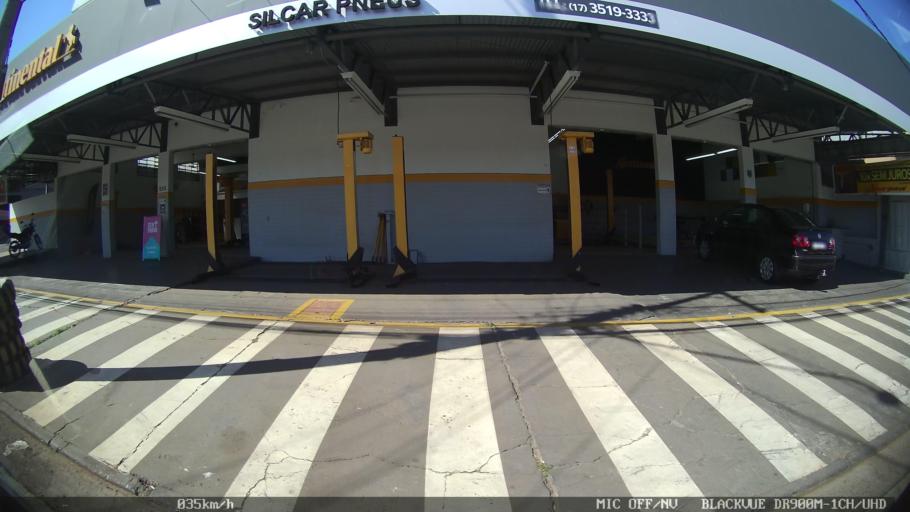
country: BR
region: Sao Paulo
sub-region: Sao Jose Do Rio Preto
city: Sao Jose do Rio Preto
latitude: -20.7963
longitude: -49.3918
